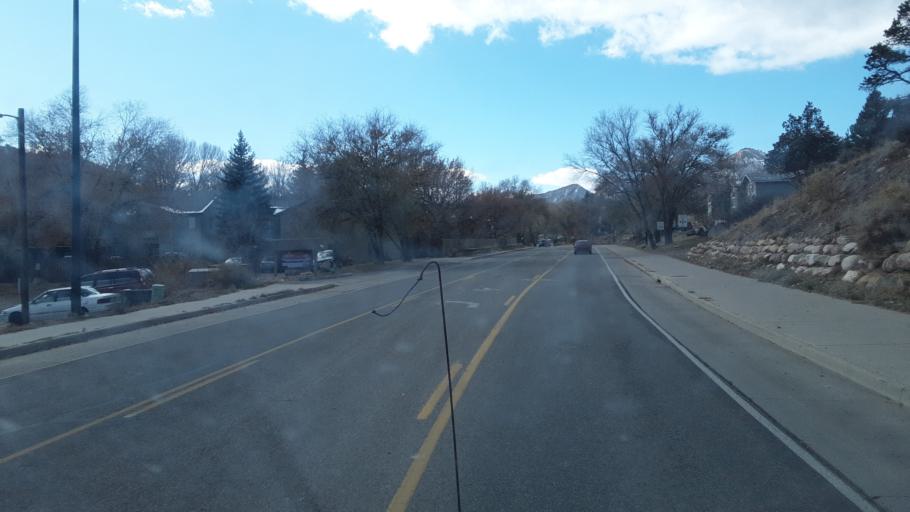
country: US
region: Colorado
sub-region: La Plata County
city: Durango
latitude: 37.2957
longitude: -107.8545
